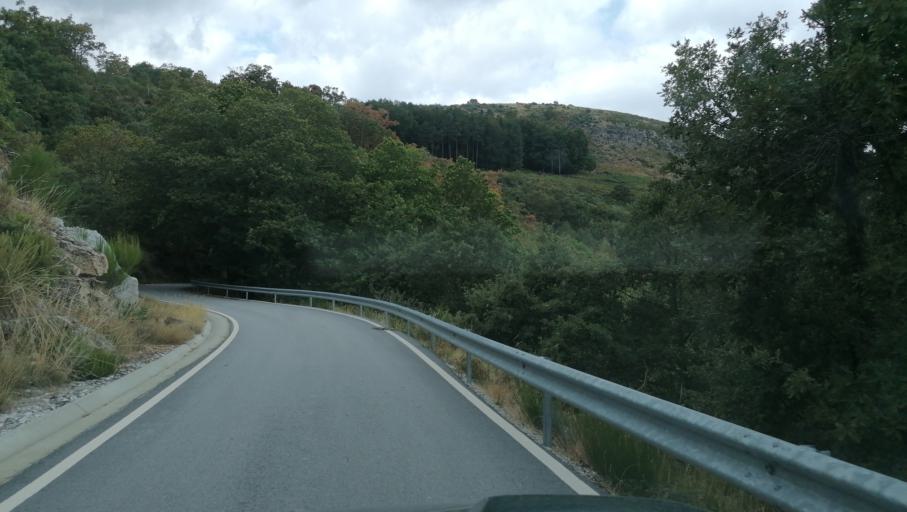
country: PT
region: Vila Real
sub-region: Vila Pouca de Aguiar
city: Vila Pouca de Aguiar
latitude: 41.5517
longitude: -7.6566
